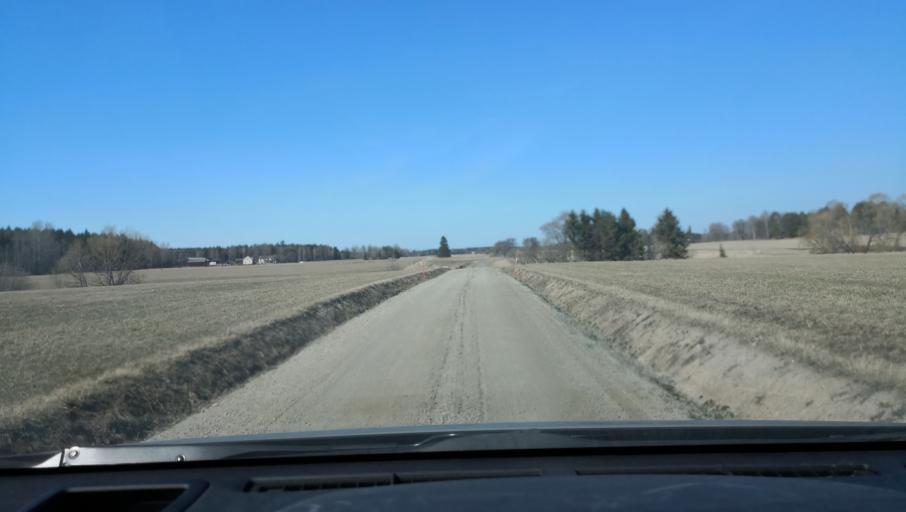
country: SE
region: Vaestmanland
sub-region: Sala Kommun
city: Sala
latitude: 59.8779
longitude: 16.5325
